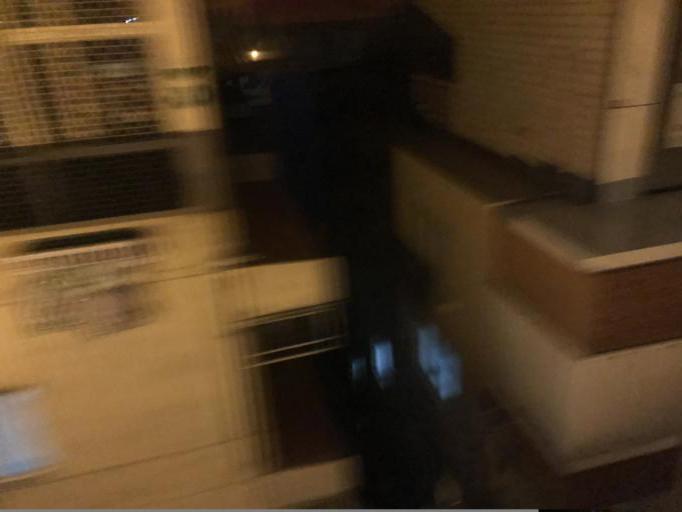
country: TR
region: Istanbul
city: Maltepe
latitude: 40.9240
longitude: 29.1435
